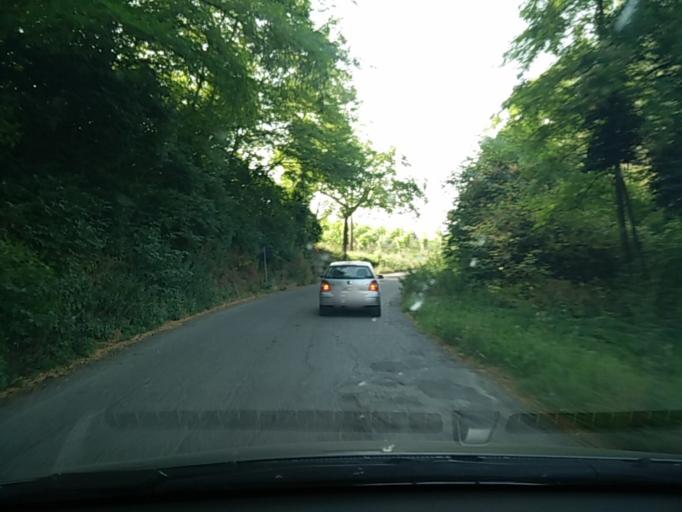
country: IT
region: Lombardy
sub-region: Provincia di Pavia
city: Susella
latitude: 44.9396
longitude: 9.1150
